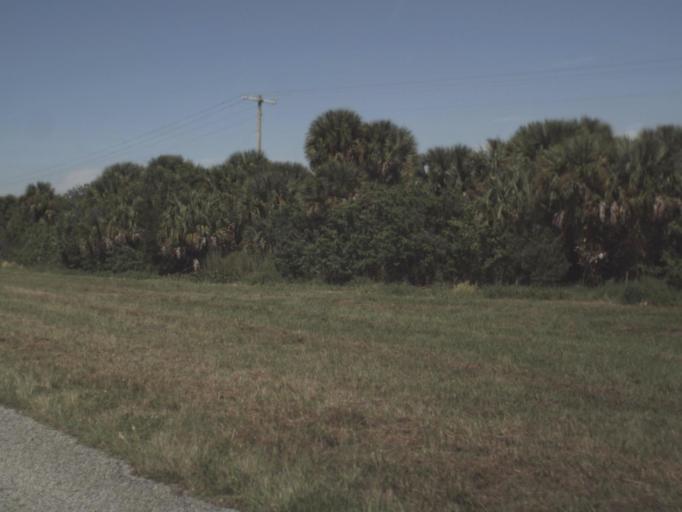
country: US
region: Florida
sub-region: Glades County
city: Moore Haven
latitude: 26.8358
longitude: -81.1921
